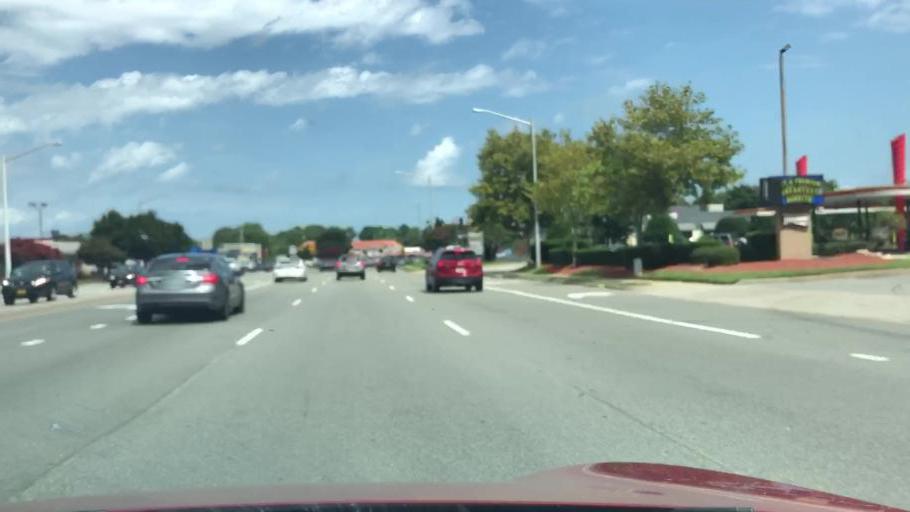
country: US
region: Virginia
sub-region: City of Chesapeake
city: Chesapeake
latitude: 36.8725
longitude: -76.1340
